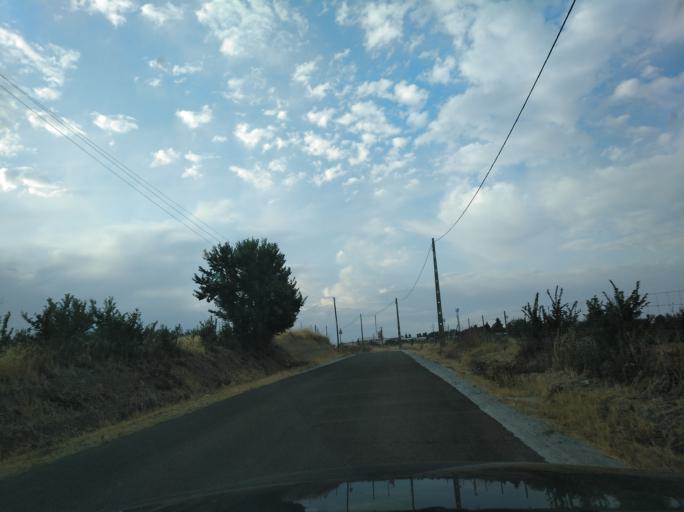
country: PT
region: Portalegre
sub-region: Campo Maior
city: Campo Maior
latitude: 39.0070
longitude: -7.0613
